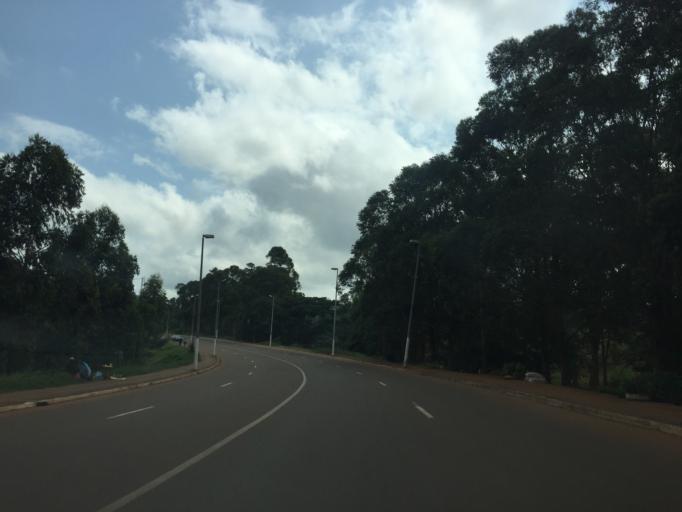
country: CM
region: Centre
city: Yaounde
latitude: 3.9010
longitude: 11.5046
